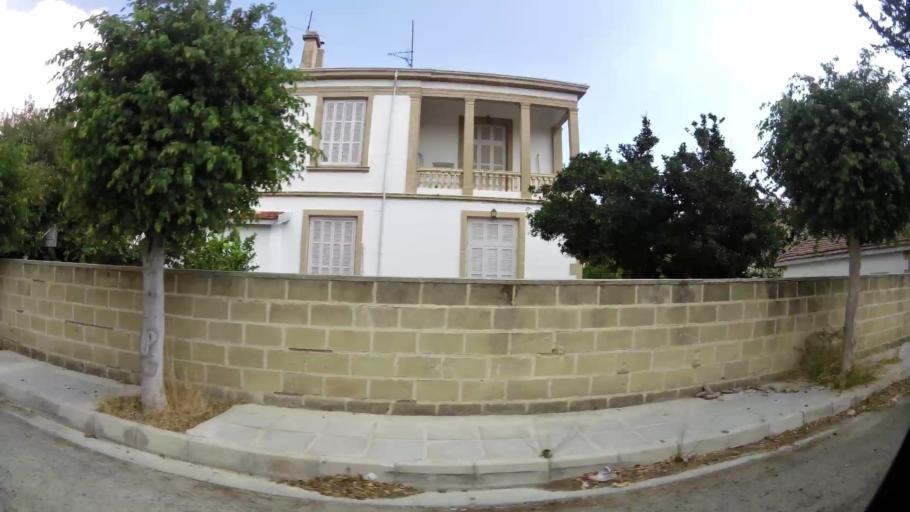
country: CY
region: Larnaka
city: Larnaca
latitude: 34.9153
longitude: 33.6240
